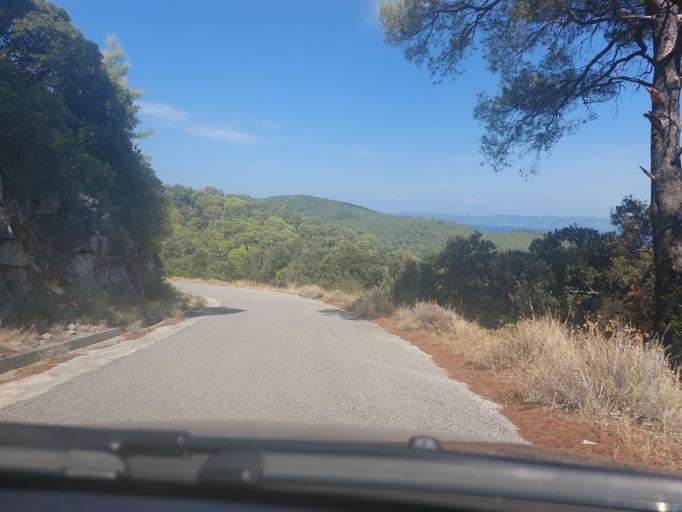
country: HR
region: Dubrovacko-Neretvanska
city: Smokvica
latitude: 42.7482
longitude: 16.8463
